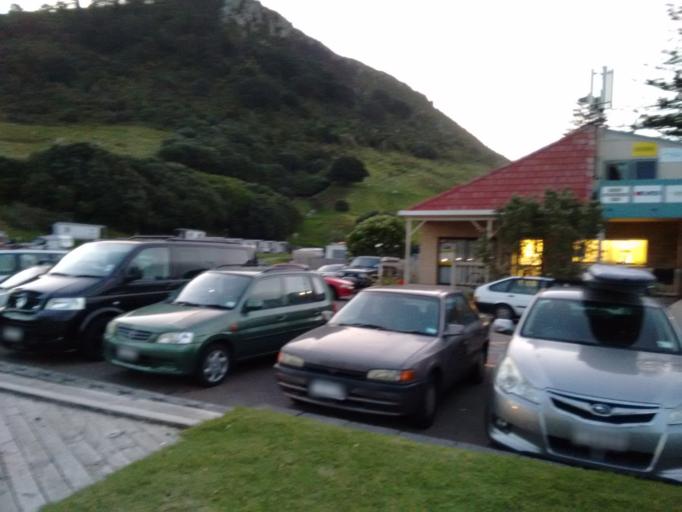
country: NZ
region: Bay of Plenty
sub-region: Tauranga City
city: Tauranga
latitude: -37.6314
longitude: 176.1771
